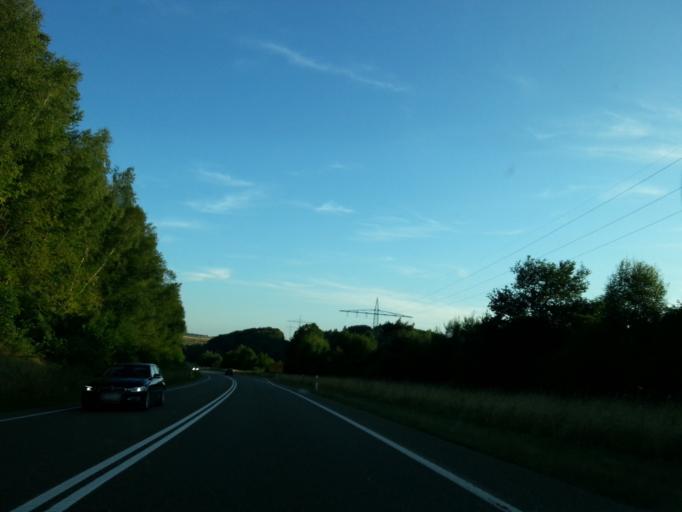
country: DE
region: Rheinland-Pfalz
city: Donsieders
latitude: 49.2629
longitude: 7.5964
